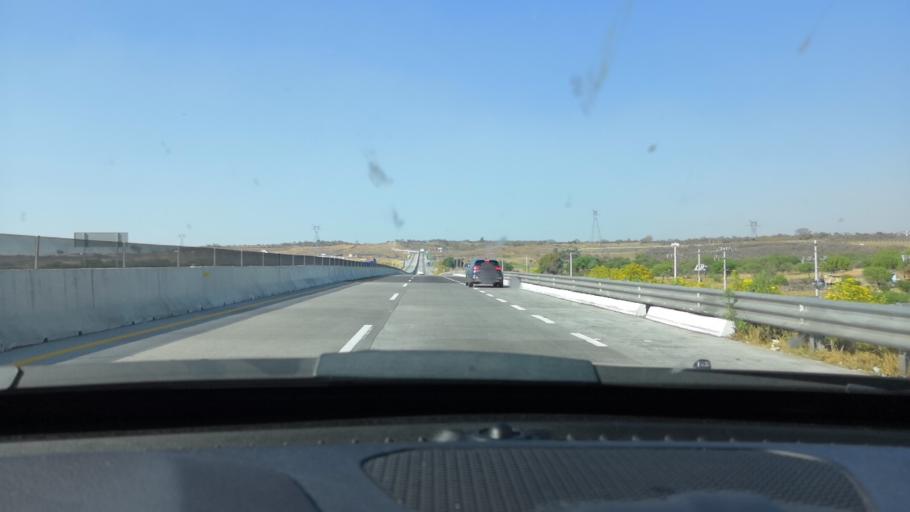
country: MX
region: Jalisco
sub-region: Zapotlanejo
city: La Mezquitera
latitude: 20.5756
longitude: -103.1009
